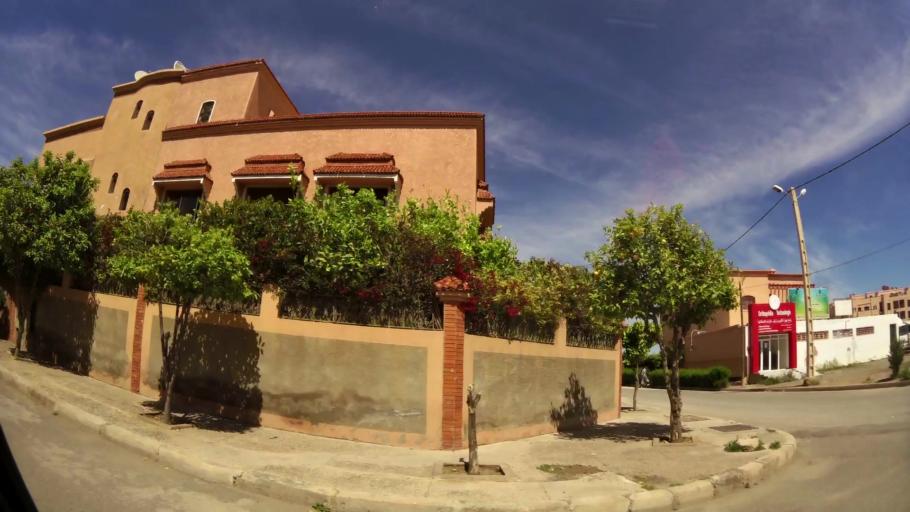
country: MA
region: Marrakech-Tensift-Al Haouz
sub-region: Marrakech
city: Marrakesh
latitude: 31.6637
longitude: -7.9917
